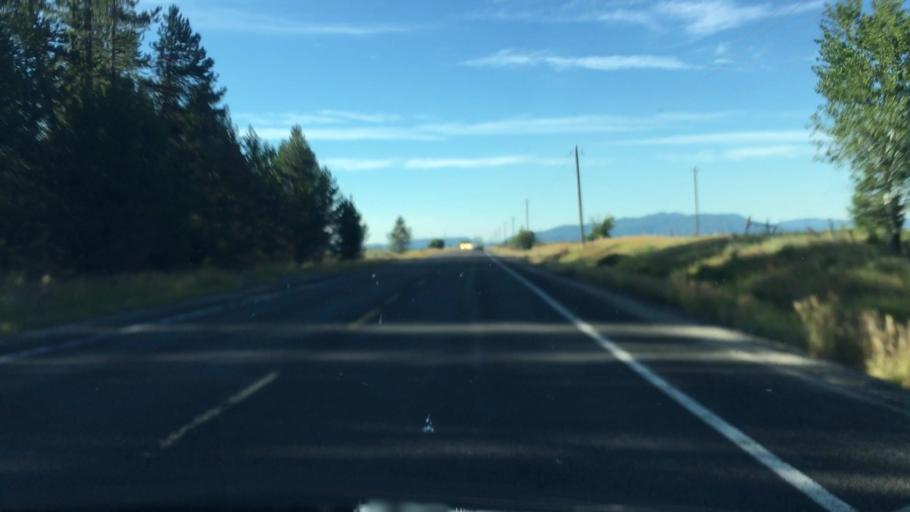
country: US
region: Idaho
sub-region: Valley County
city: Cascade
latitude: 44.4130
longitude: -115.9998
